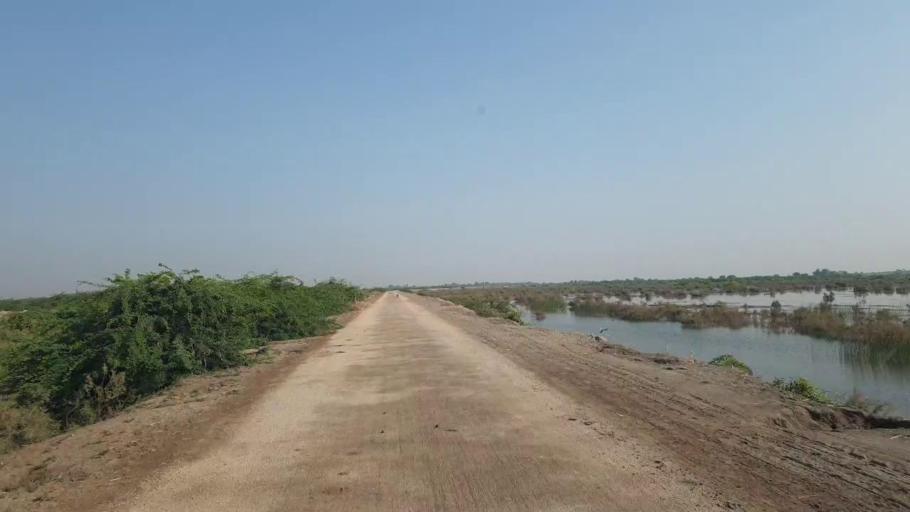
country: PK
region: Sindh
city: Badin
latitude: 24.4812
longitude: 68.7451
